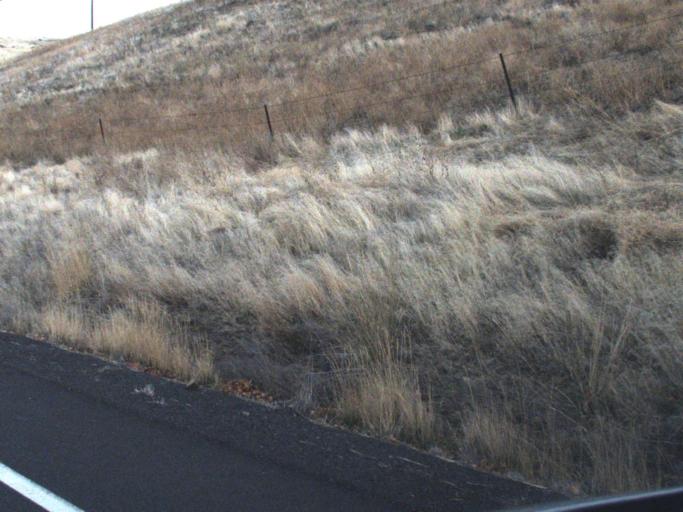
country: US
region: Washington
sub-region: Garfield County
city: Pomeroy
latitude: 46.4580
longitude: -117.4722
